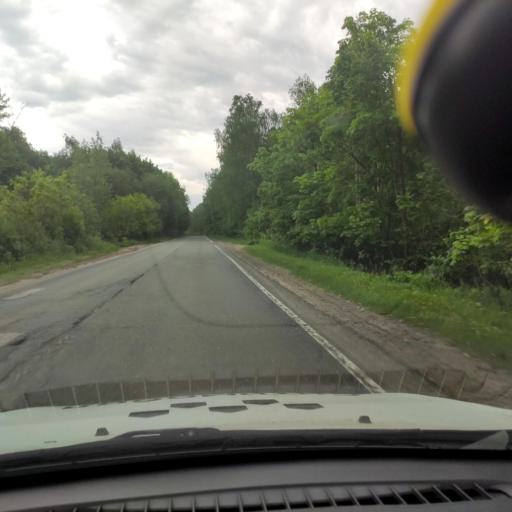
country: RU
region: Samara
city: Zhigulevsk
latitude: 53.3389
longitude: 49.5040
